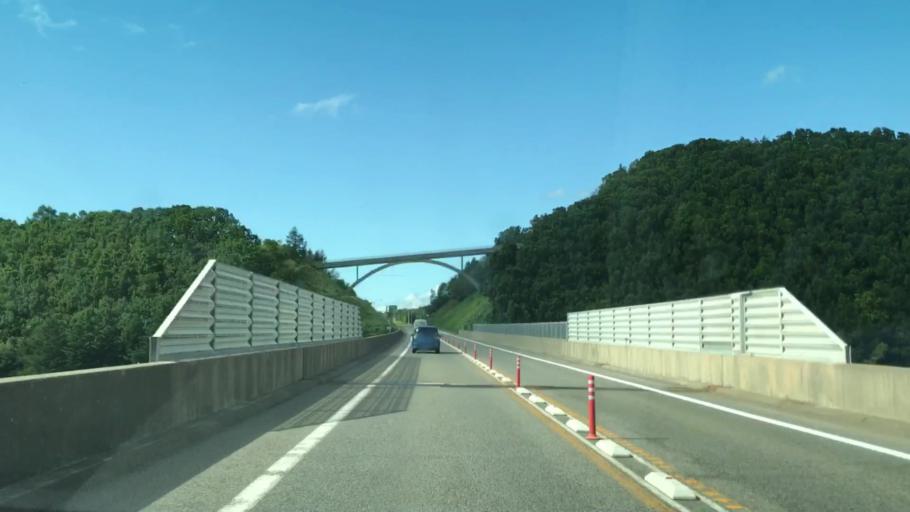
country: JP
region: Hokkaido
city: Date
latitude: 42.4595
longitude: 140.9117
